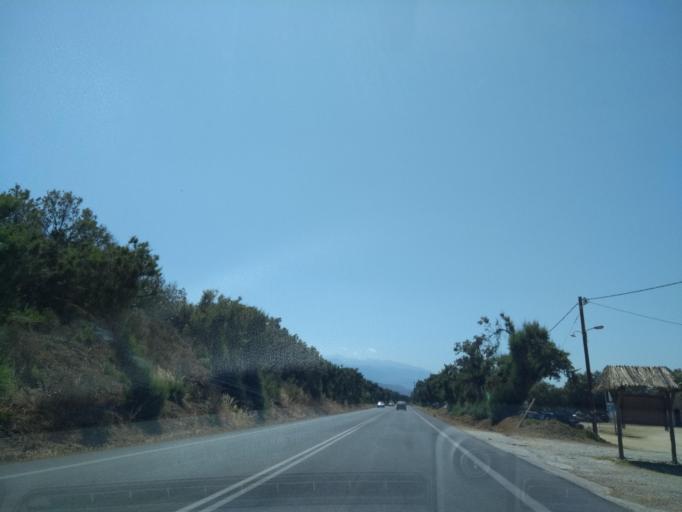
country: GR
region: Crete
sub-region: Nomos Chanias
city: Georgioupolis
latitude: 35.3506
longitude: 24.3385
